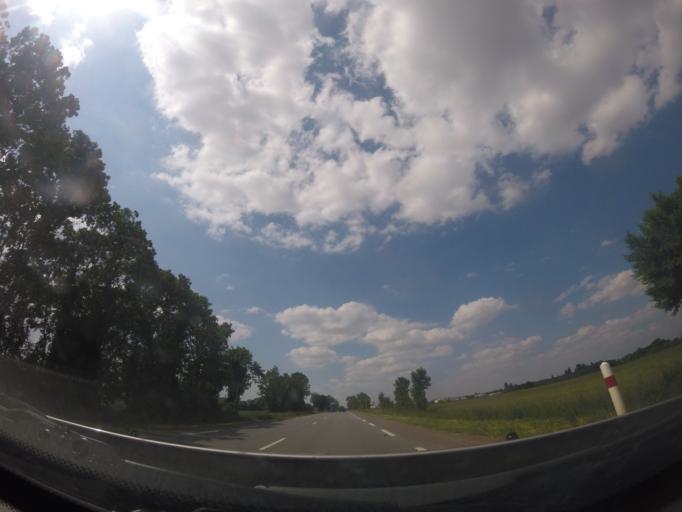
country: FR
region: Poitou-Charentes
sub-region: Departement de la Charente-Maritime
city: Saint-Porchaire
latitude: 45.8509
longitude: -0.8235
